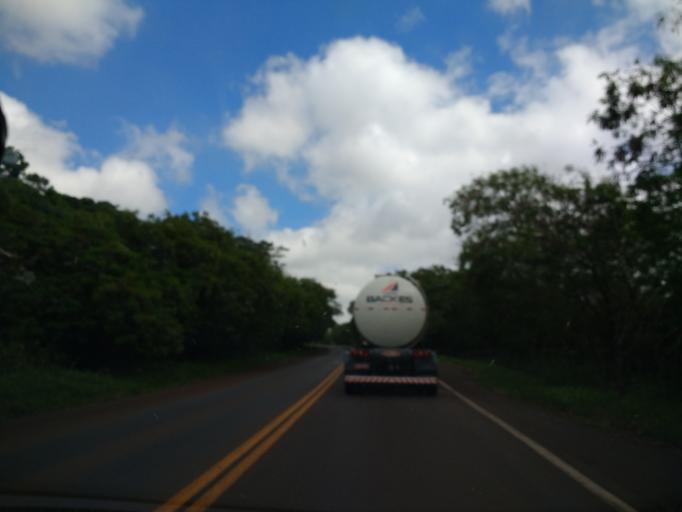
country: BR
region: Parana
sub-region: Cruzeiro Do Oeste
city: Cruzeiro do Oeste
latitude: -23.7895
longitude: -53.0341
